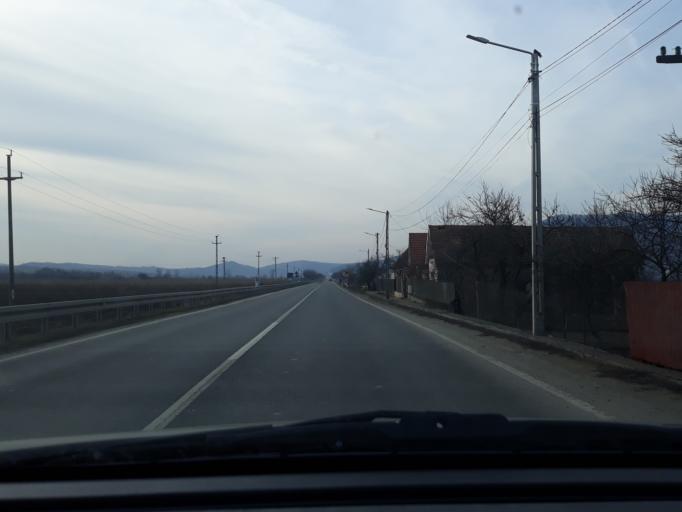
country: RO
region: Salaj
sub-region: Comuna Periceiu
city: Periceiu
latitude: 47.2274
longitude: 22.8565
